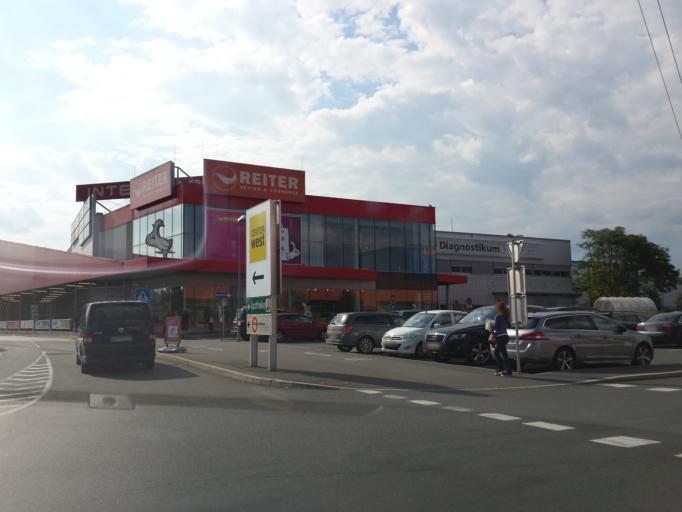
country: AT
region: Styria
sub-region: Graz Stadt
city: Wetzelsdorf
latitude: 47.0331
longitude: 15.4193
